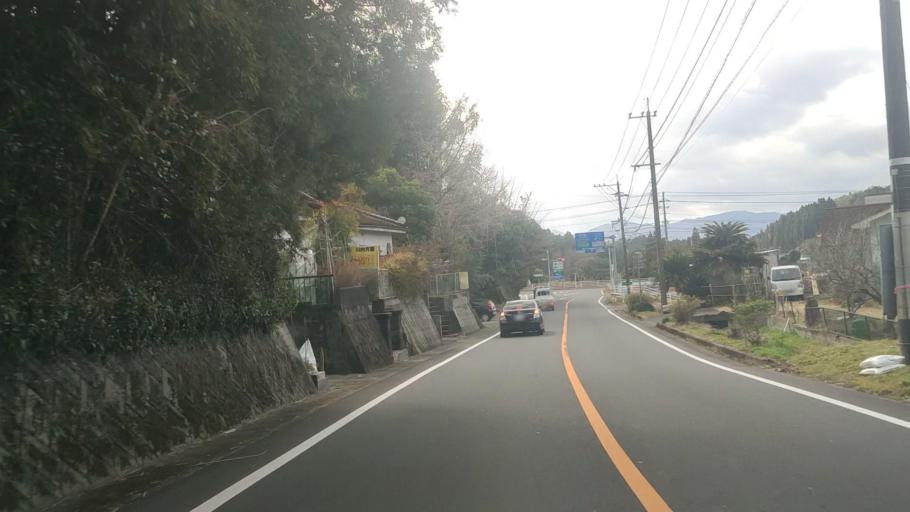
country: JP
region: Kagoshima
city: Kajiki
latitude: 31.7570
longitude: 130.6785
